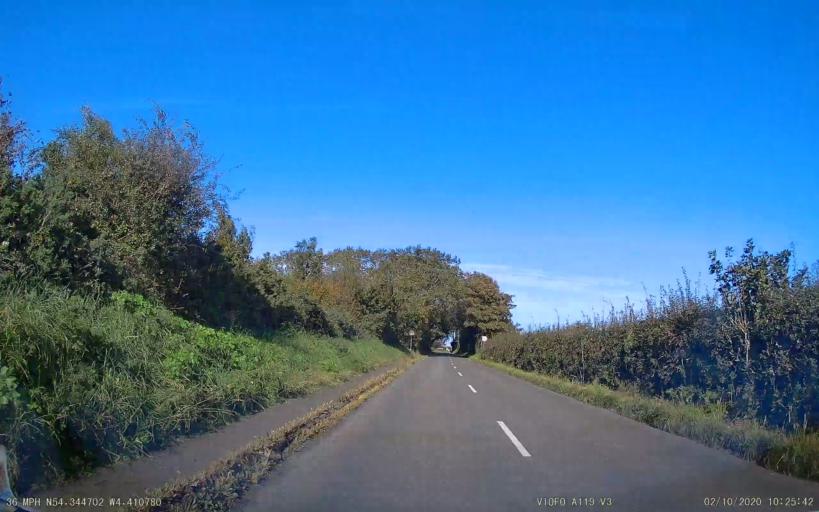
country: IM
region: Ramsey
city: Ramsey
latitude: 54.3447
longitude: -4.4108
